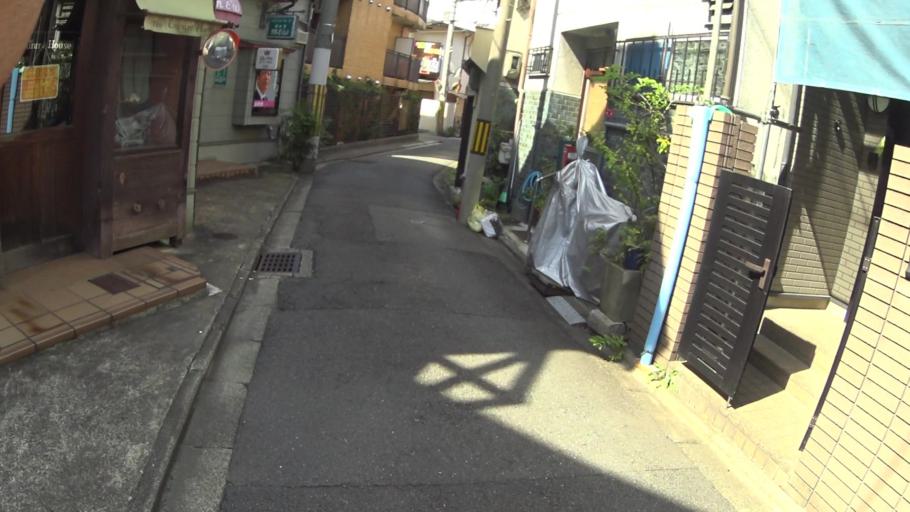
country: JP
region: Kyoto
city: Kyoto
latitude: 34.9965
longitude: 135.7754
